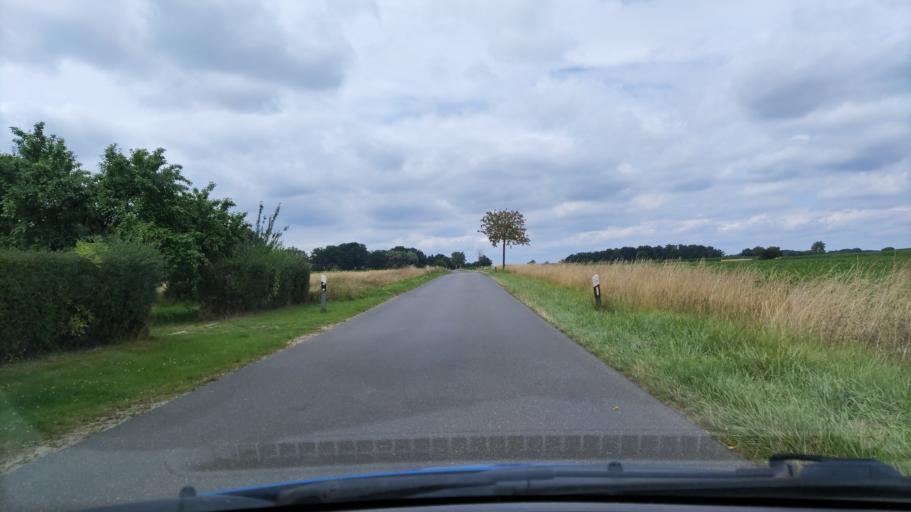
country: DE
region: Lower Saxony
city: Weste
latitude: 53.0649
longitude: 10.6979
